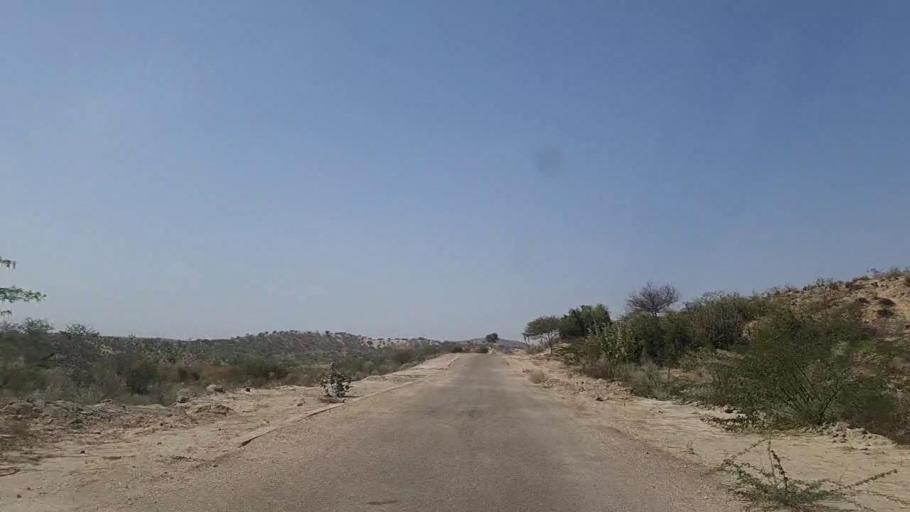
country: PK
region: Sindh
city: Diplo
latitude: 24.5419
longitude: 69.4108
